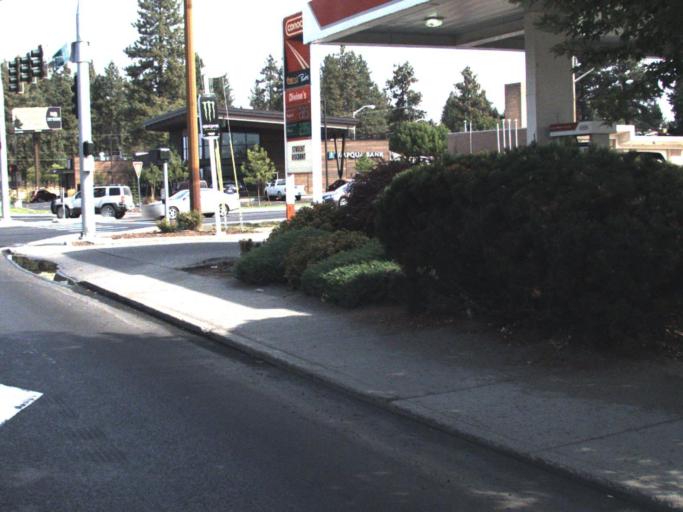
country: US
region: Washington
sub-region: Spokane County
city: Country Homes
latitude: 47.7509
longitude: -117.4110
